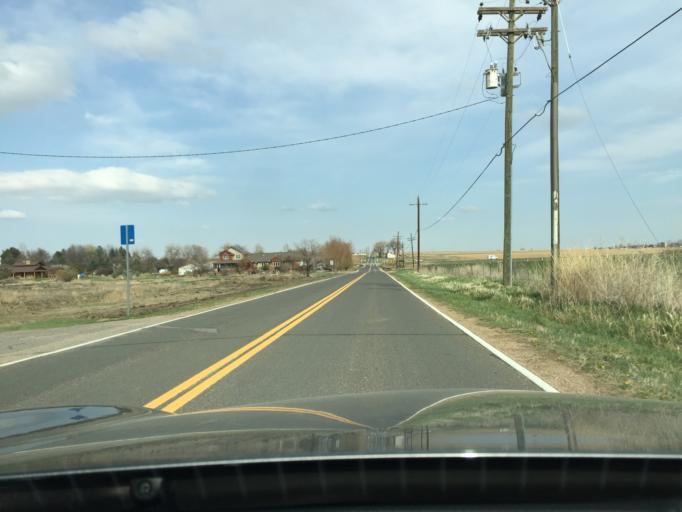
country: US
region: Colorado
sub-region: Boulder County
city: Longmont
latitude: 40.1162
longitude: -105.1073
